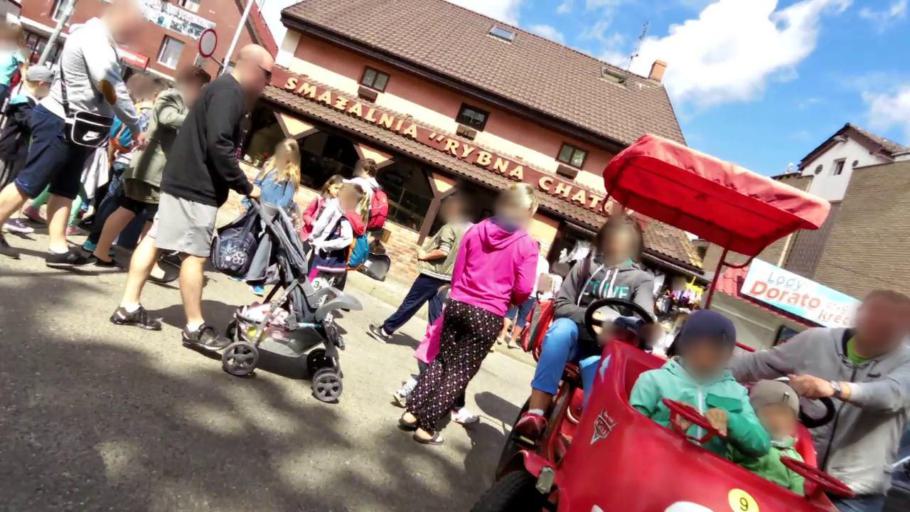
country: PL
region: West Pomeranian Voivodeship
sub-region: Powiat slawienski
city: Darlowo
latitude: 54.4396
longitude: 16.3806
